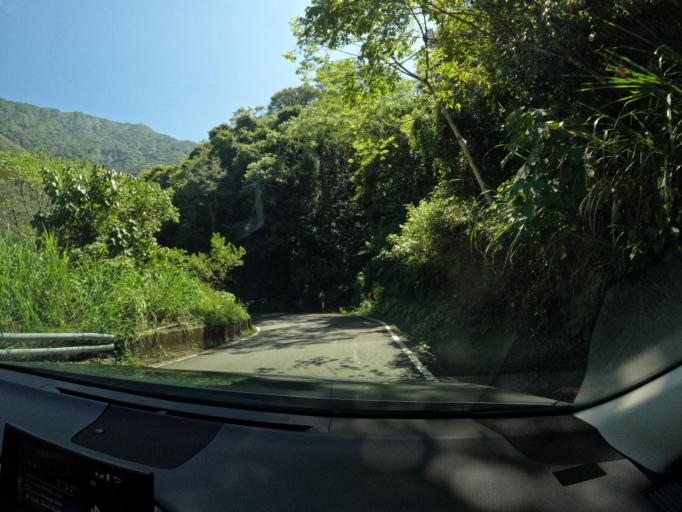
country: TW
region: Taiwan
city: Yujing
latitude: 23.2609
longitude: 120.8445
